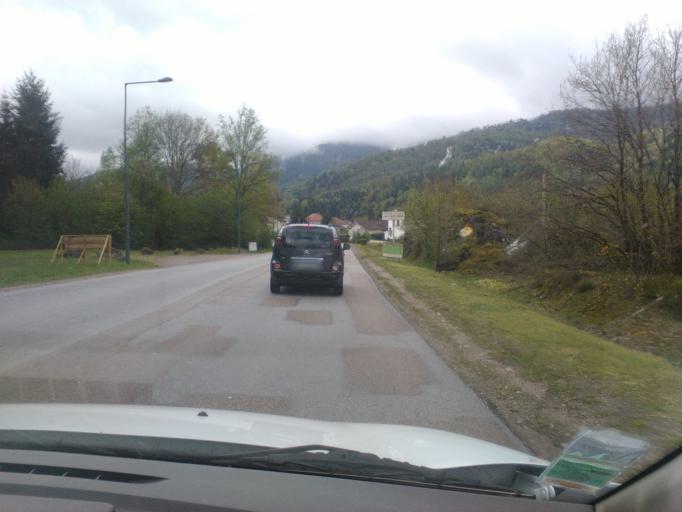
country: FR
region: Lorraine
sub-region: Departement des Vosges
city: Vagney
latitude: 47.9745
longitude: 6.7283
